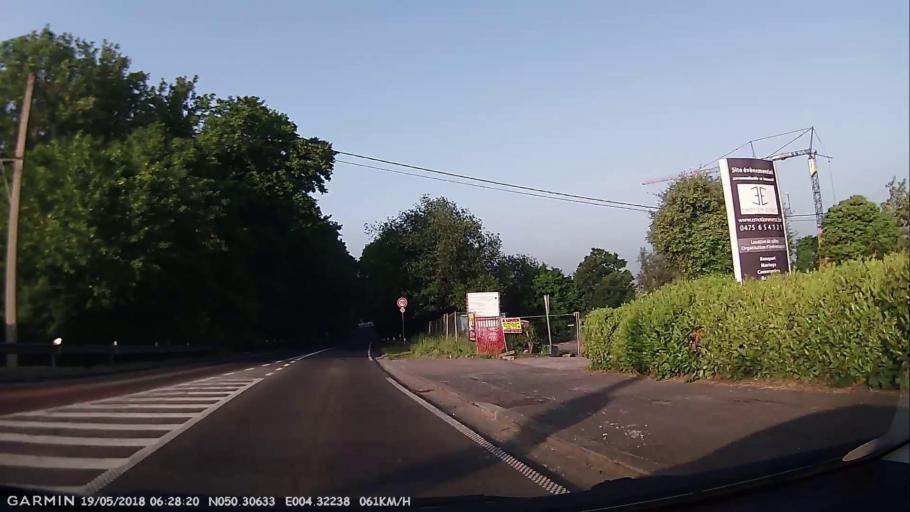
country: BE
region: Wallonia
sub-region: Province du Hainaut
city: Thuin
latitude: 50.3063
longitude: 4.3224
